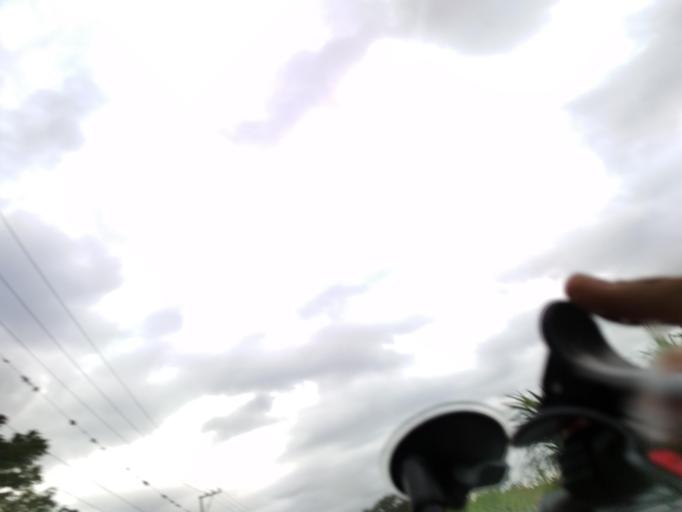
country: MX
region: Veracruz
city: El Castillo
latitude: 19.5849
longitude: -96.8358
